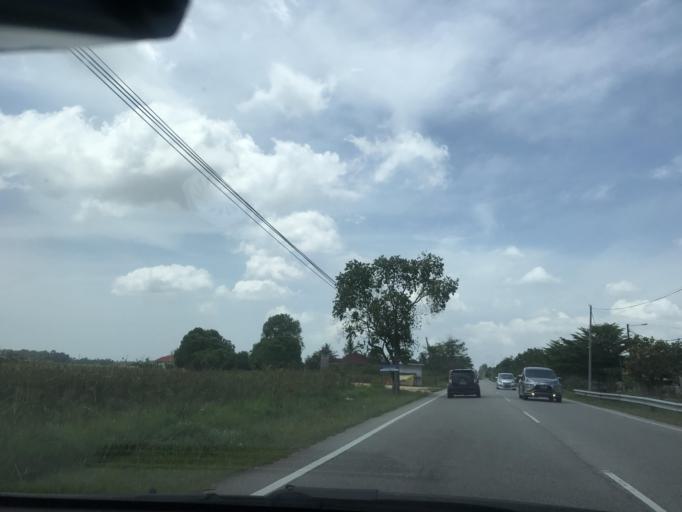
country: MY
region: Kelantan
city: Kota Bharu
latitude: 6.1505
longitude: 102.2109
